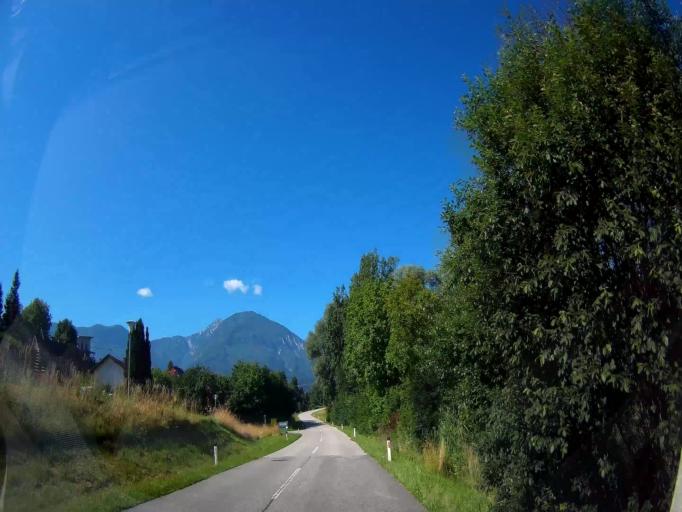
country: AT
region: Carinthia
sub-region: Politischer Bezirk Volkermarkt
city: Gallizien
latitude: 46.5778
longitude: 14.5104
